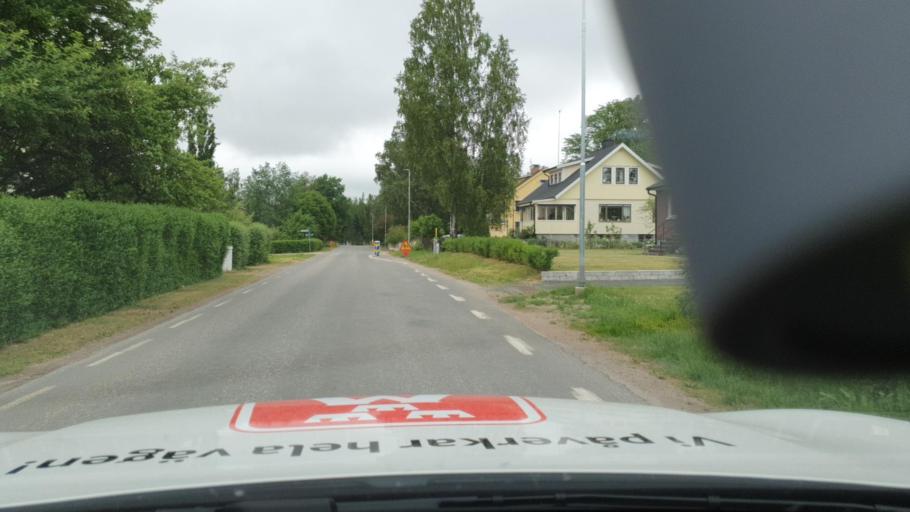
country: SE
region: Vaestra Goetaland
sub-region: Tibro Kommun
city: Tibro
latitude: 58.3694
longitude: 14.0493
